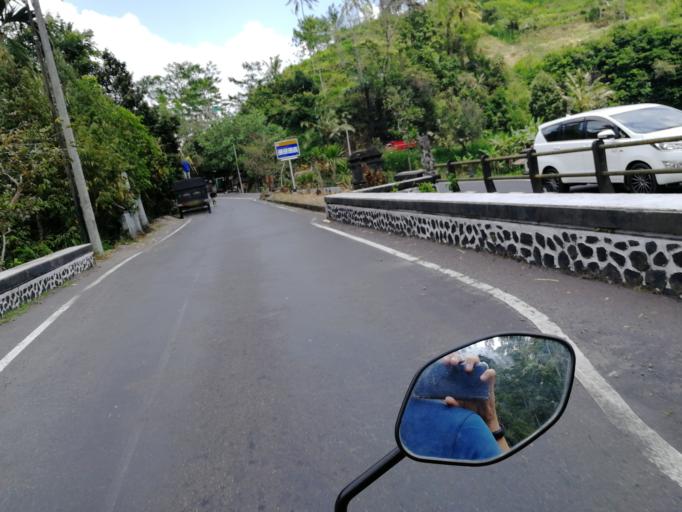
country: ID
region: Bali
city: Banjar Geriana Kangin
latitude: -8.4238
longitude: 115.4383
